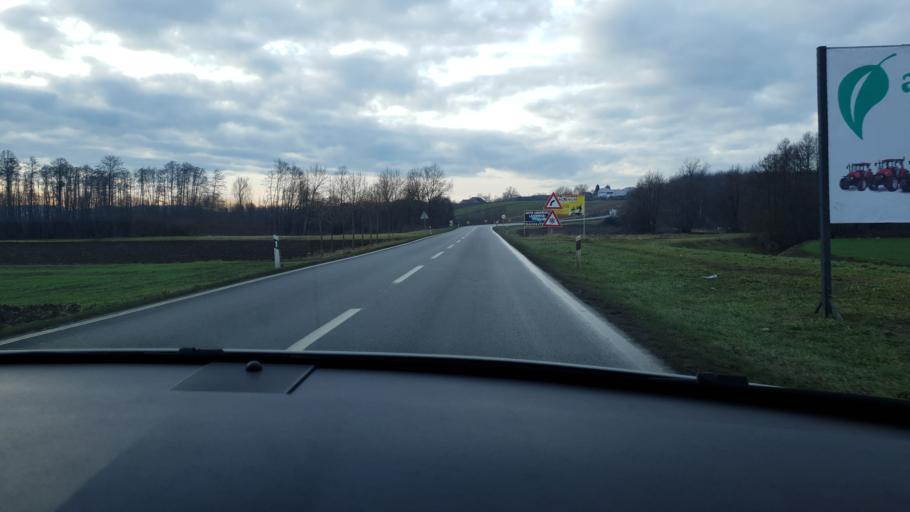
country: HR
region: Pozesko-Slavonska
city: Jaksic
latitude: 45.3555
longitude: 17.7519
